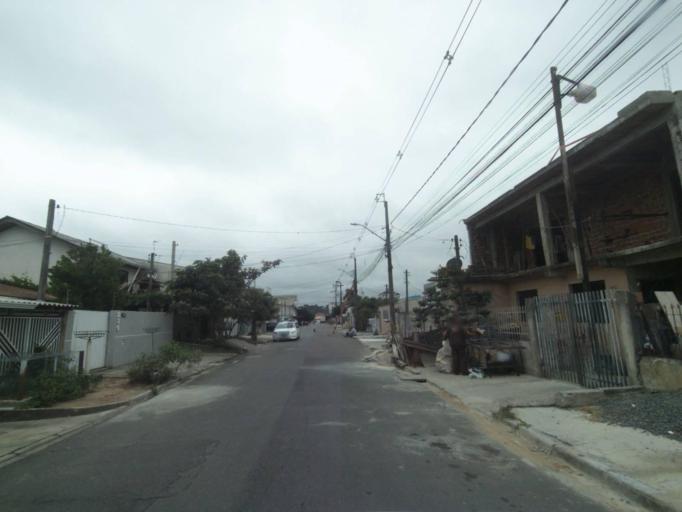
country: BR
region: Parana
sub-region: Araucaria
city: Araucaria
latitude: -25.5319
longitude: -49.3386
